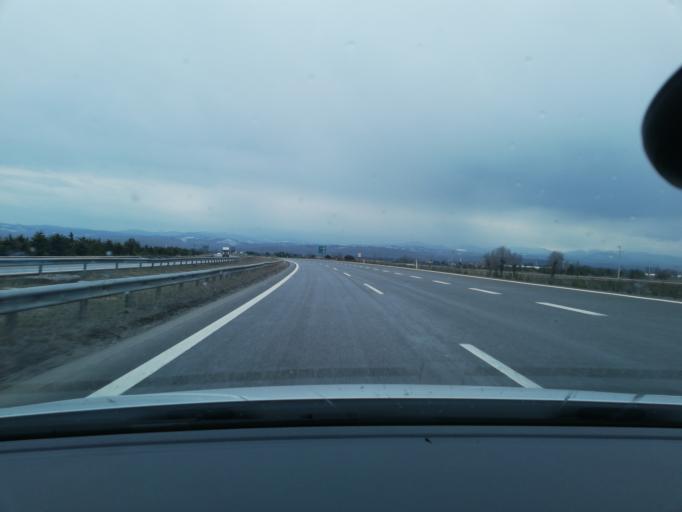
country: TR
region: Bolu
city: Gerede
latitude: 40.7745
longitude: 32.2059
